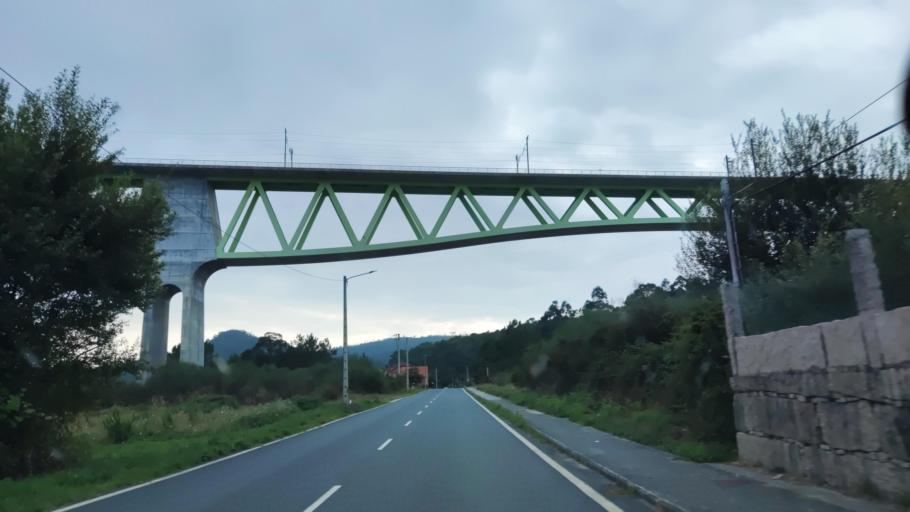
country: ES
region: Galicia
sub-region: Provincia de Pontevedra
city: Catoira
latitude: 42.6727
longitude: -8.7335
